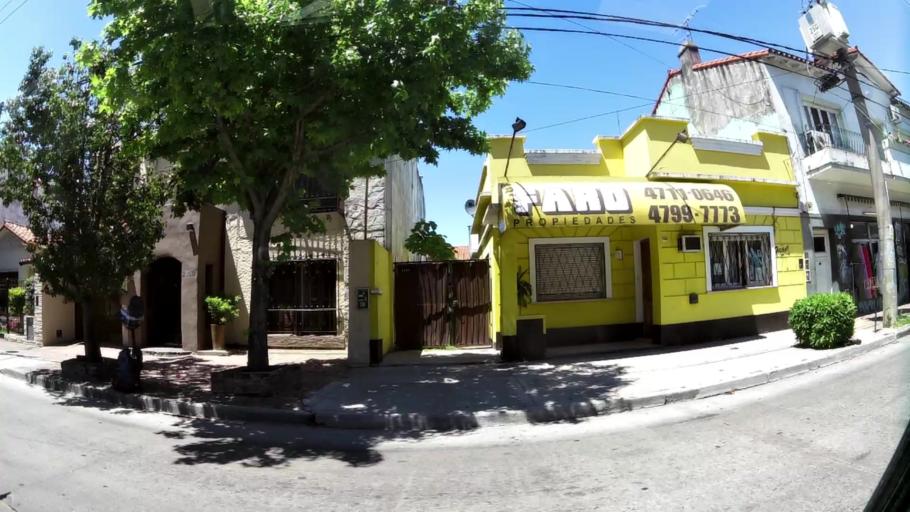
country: AR
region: Buenos Aires
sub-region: Partido de Vicente Lopez
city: Olivos
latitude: -34.5033
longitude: -58.5099
